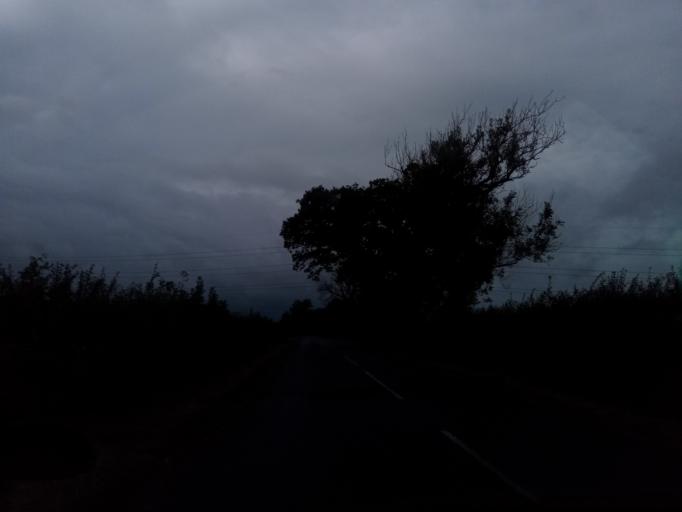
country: GB
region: Scotland
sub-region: The Scottish Borders
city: Duns
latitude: 55.7445
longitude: -2.3189
